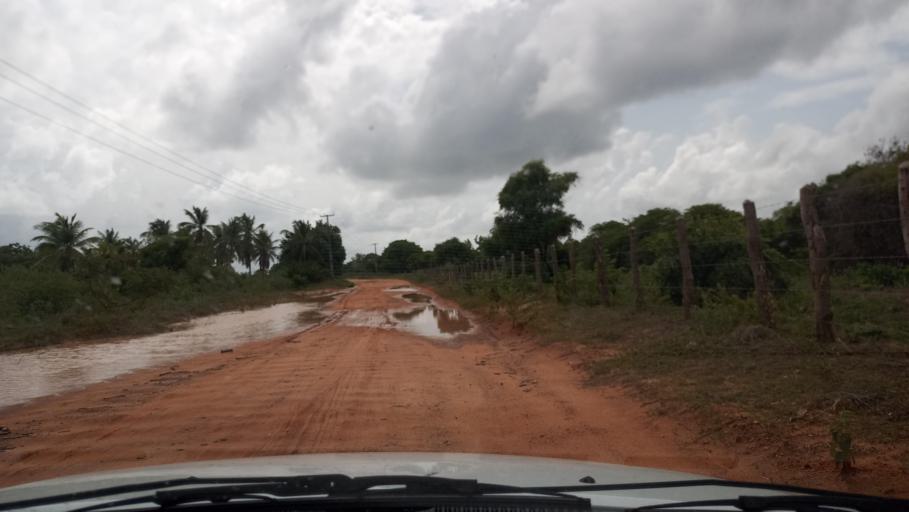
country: BR
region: Rio Grande do Norte
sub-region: Maxaranguape
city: Sao Miguel
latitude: -5.4841
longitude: -35.3128
